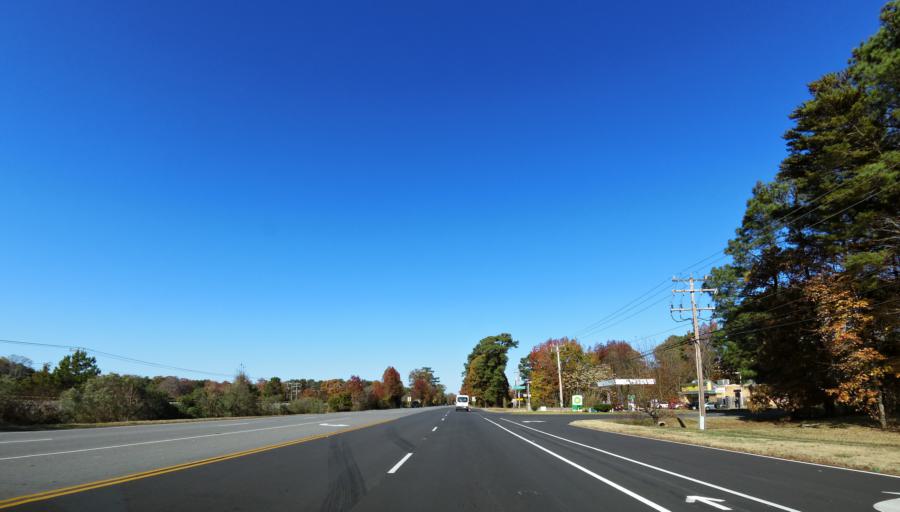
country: US
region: Virginia
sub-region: City of Williamsburg
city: Williamsburg
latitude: 37.2432
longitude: -76.6509
